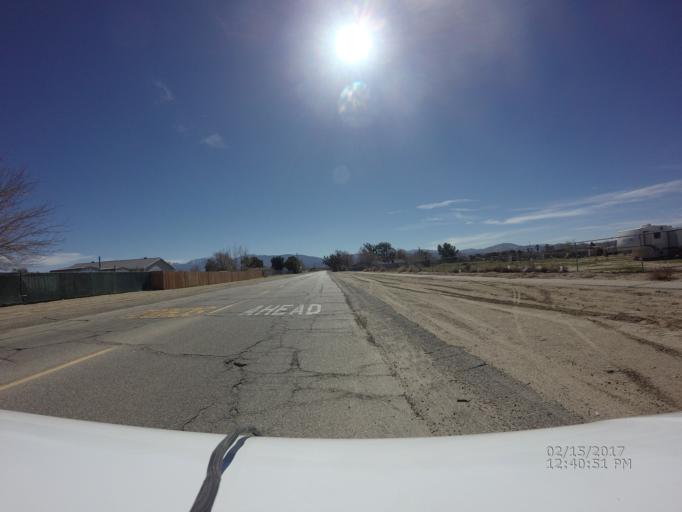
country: US
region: California
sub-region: Los Angeles County
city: Littlerock
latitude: 34.5776
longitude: -117.9608
